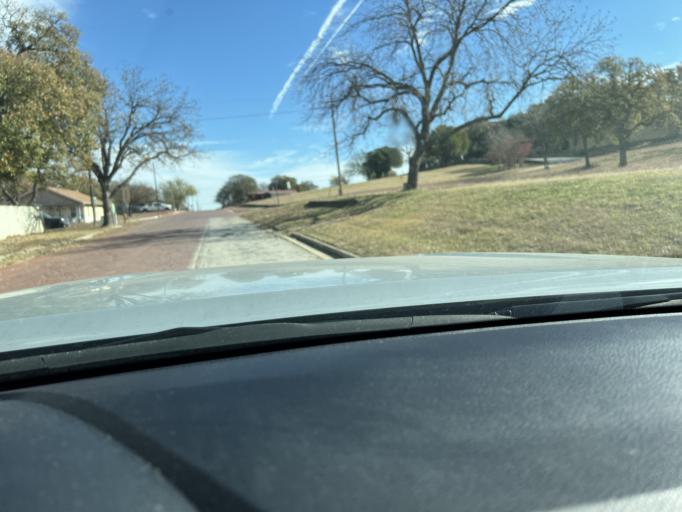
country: US
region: Texas
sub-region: Eastland County
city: Eastland
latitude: 32.3995
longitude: -98.8287
